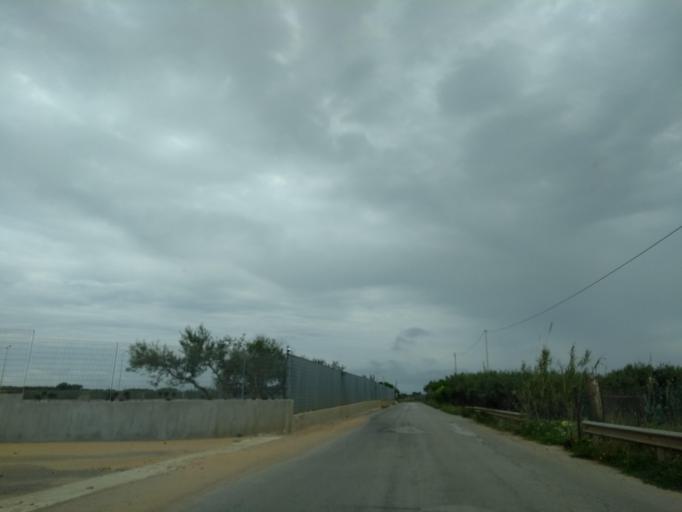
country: IT
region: Sicily
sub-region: Palermo
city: Partinico
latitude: 38.0026
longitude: 13.0681
